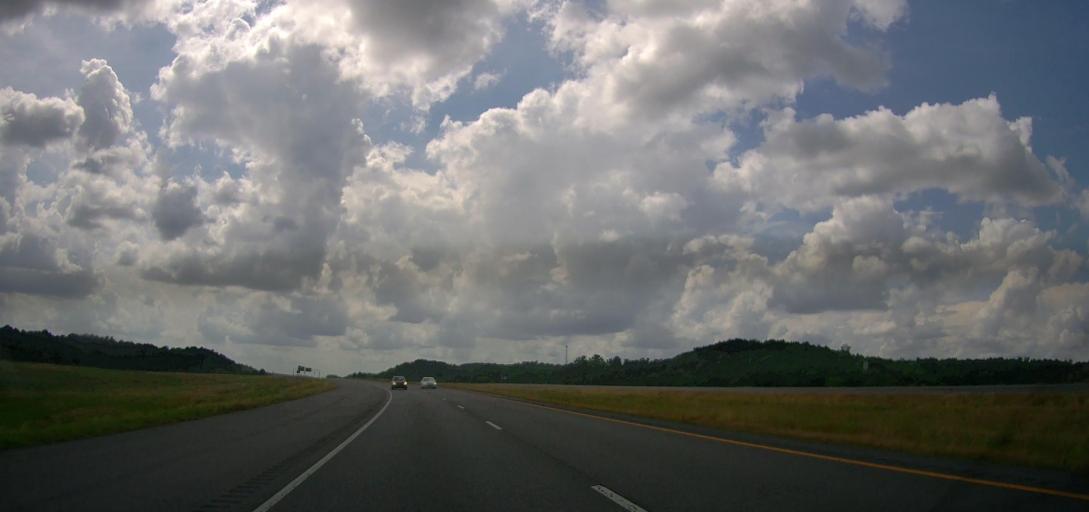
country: US
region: Alabama
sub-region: Walker County
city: Jasper
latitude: 33.8561
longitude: -87.3506
